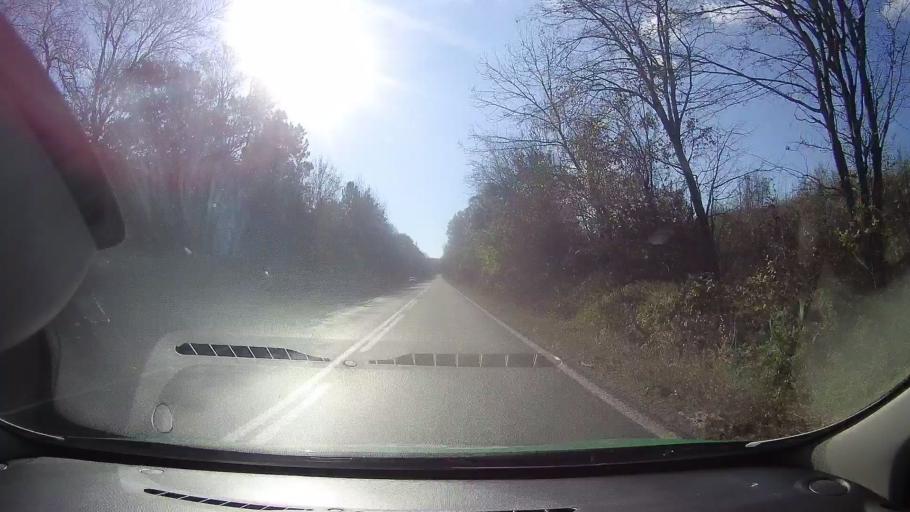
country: RO
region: Tulcea
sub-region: Oras Babadag
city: Babadag
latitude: 44.8378
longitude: 28.6957
